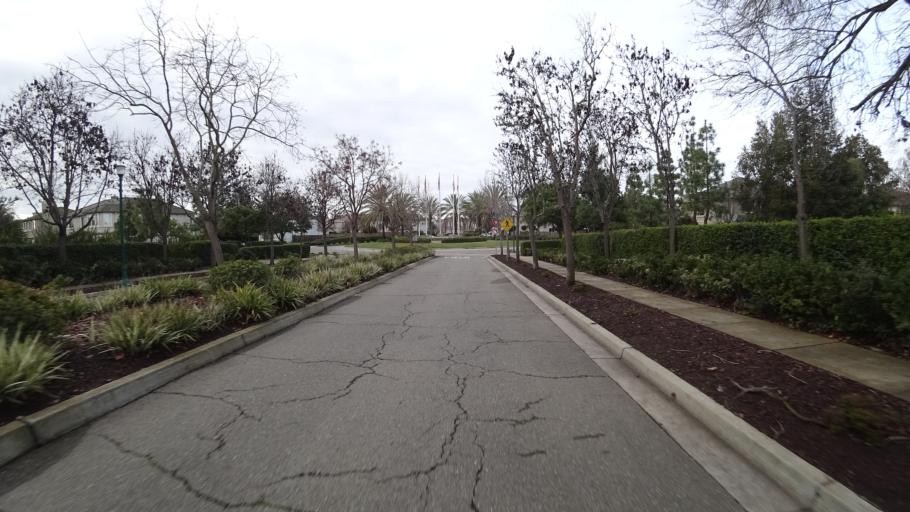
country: US
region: California
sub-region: Alameda County
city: Union City
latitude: 37.6246
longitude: -122.0432
